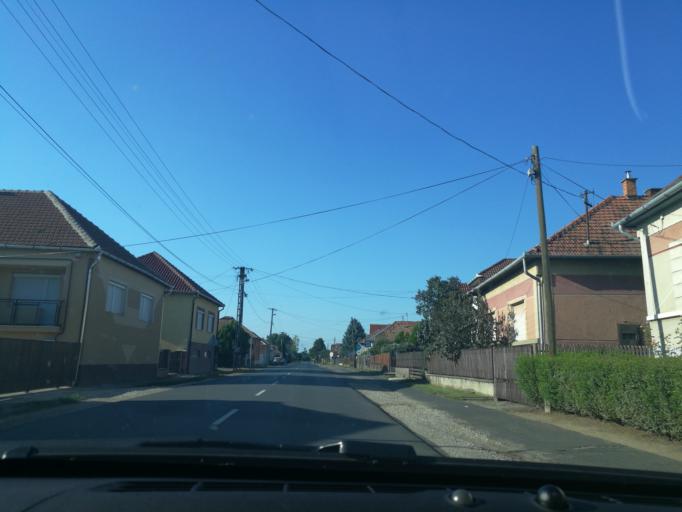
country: HU
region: Szabolcs-Szatmar-Bereg
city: Rakamaz
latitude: 48.1308
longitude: 21.4589
